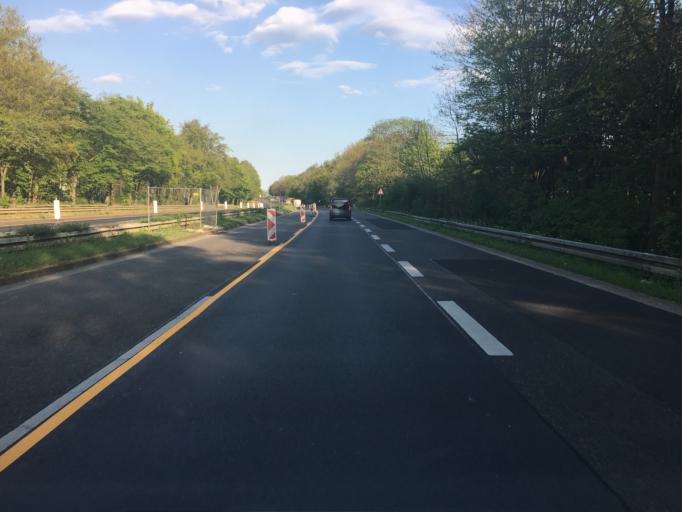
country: DE
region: North Rhine-Westphalia
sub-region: Regierungsbezirk Koln
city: Leverkusen
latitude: 51.0264
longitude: 6.9289
